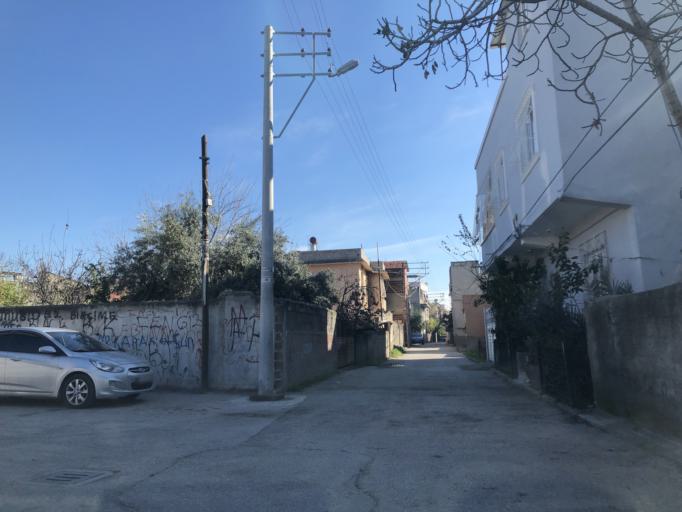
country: TR
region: Adana
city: Yuregir
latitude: 37.0055
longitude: 35.3671
